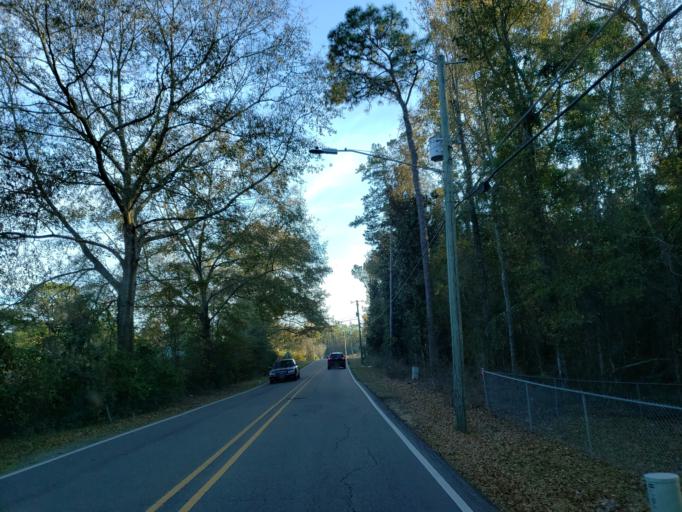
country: US
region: Mississippi
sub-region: Lamar County
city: Arnold Line
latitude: 31.3429
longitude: -89.3454
